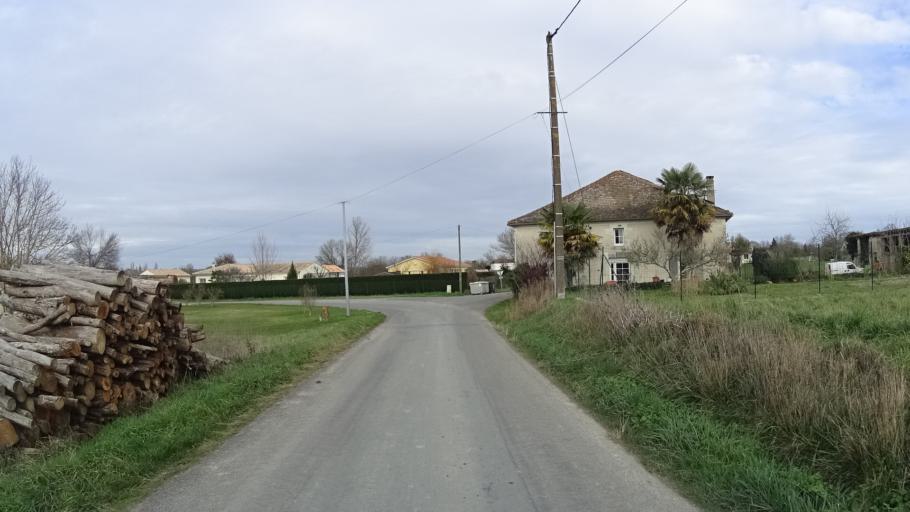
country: FR
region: Aquitaine
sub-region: Departement de la Dordogne
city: Saint-Aulaye
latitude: 45.2354
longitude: 0.1648
